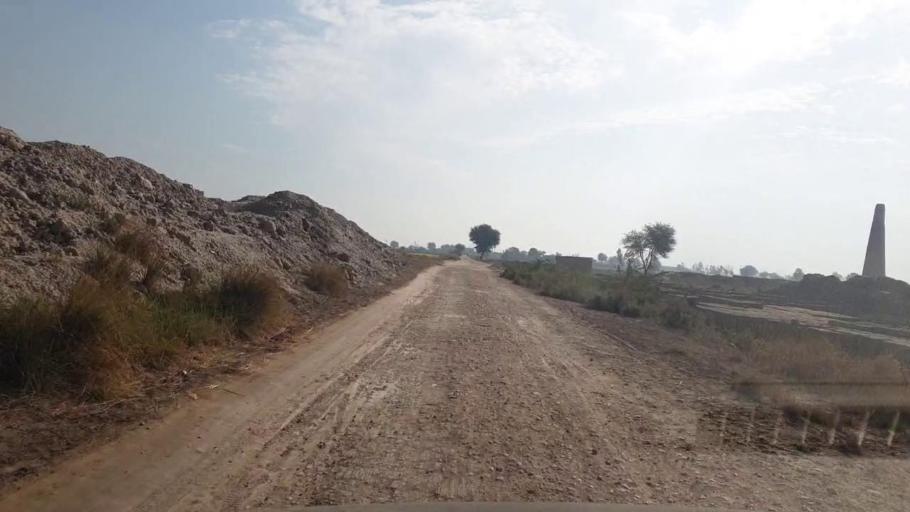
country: PK
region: Sindh
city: Hala
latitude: 25.9881
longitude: 68.3904
